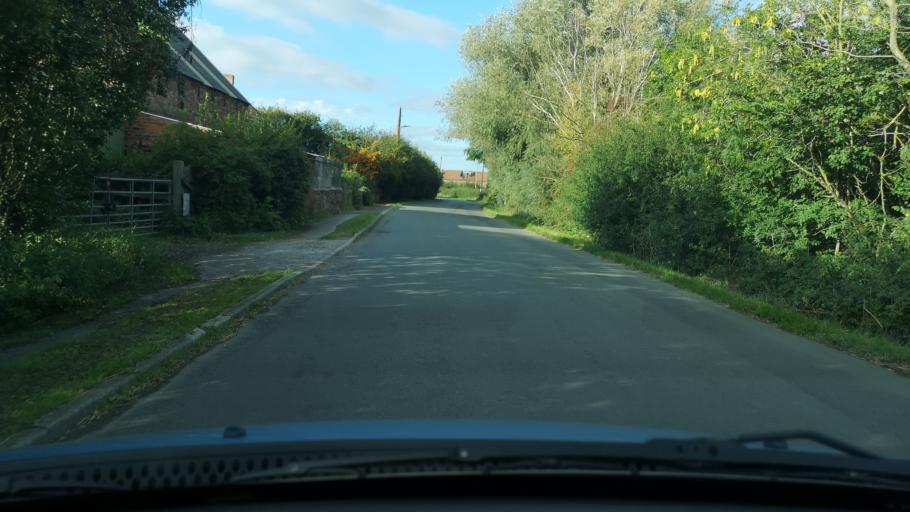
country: GB
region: England
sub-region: Doncaster
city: Stainforth
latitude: 53.6186
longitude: -1.0135
